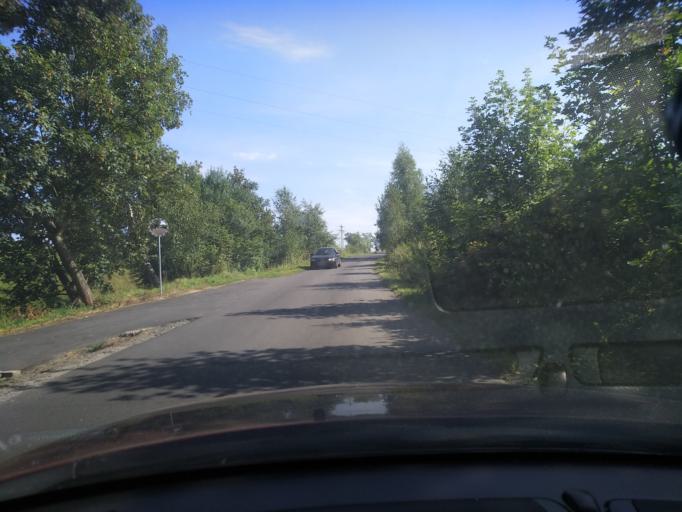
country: PL
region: Lower Silesian Voivodeship
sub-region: Powiat lubanski
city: Lesna
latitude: 51.0309
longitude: 15.2946
